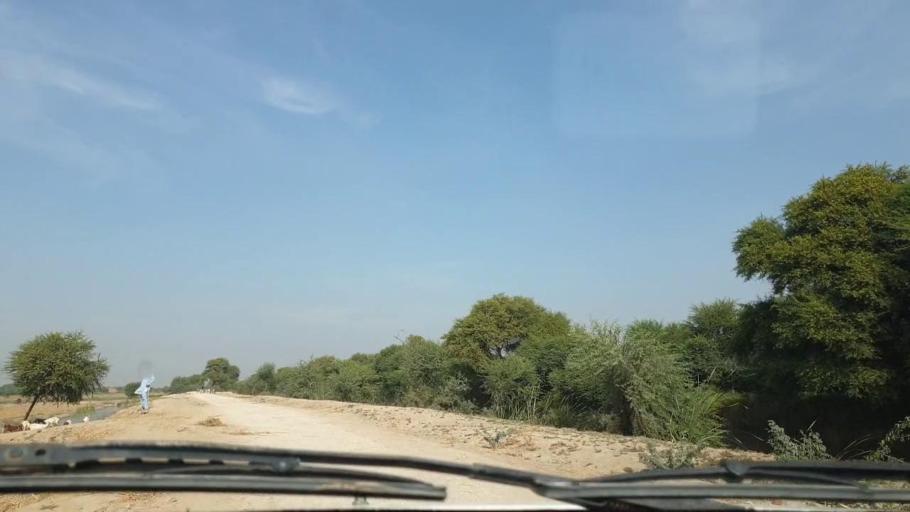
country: PK
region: Sindh
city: Bulri
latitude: 24.8918
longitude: 68.4626
